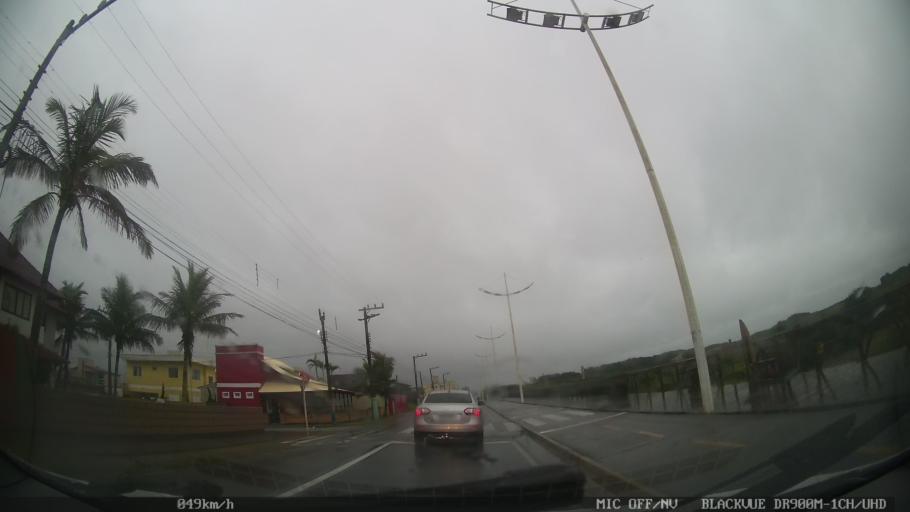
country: BR
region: Santa Catarina
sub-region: Navegantes
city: Navegantes
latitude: -26.8896
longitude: -48.6424
